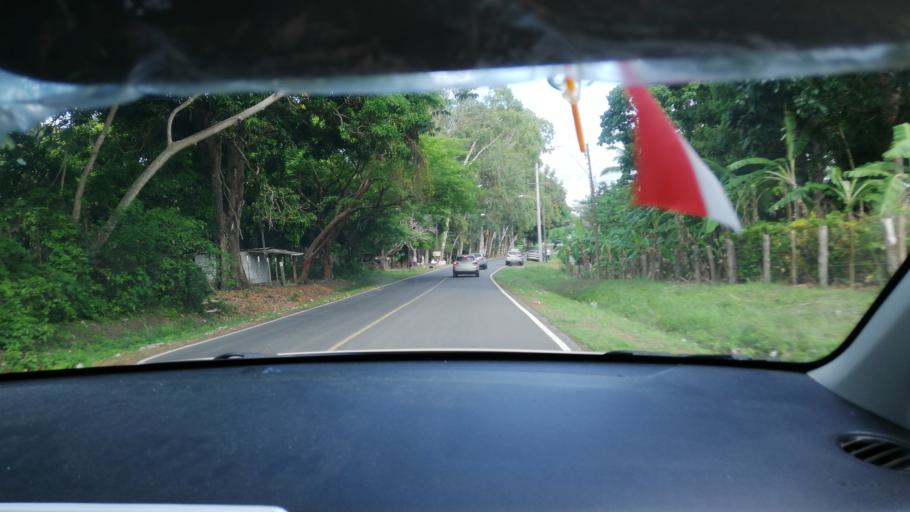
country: PA
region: Panama
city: Las Colinas
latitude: 8.5237
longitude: -80.0382
